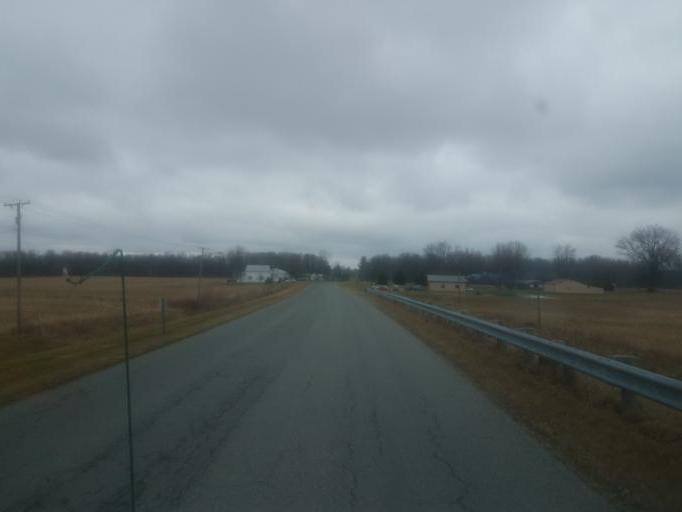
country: US
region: Ohio
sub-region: Crawford County
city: Galion
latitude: 40.7636
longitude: -82.8196
